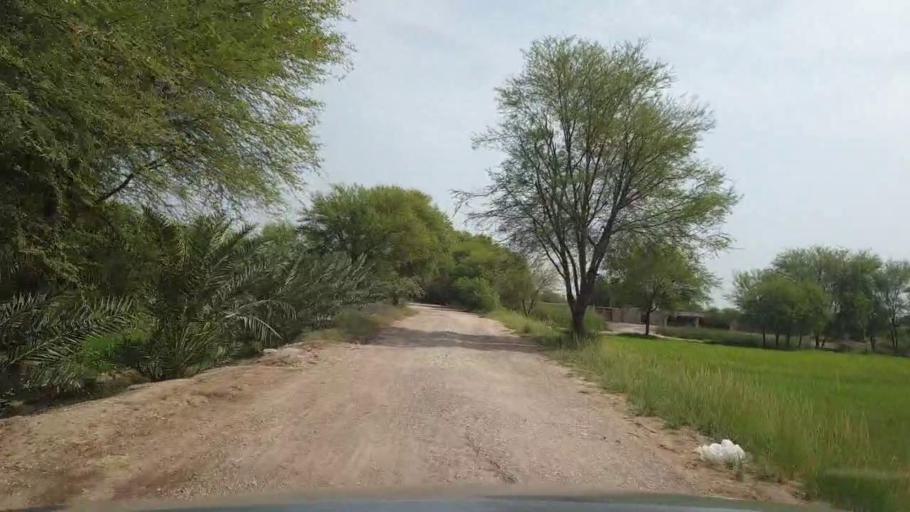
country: PK
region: Sindh
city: Rohri
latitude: 27.6527
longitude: 69.0237
